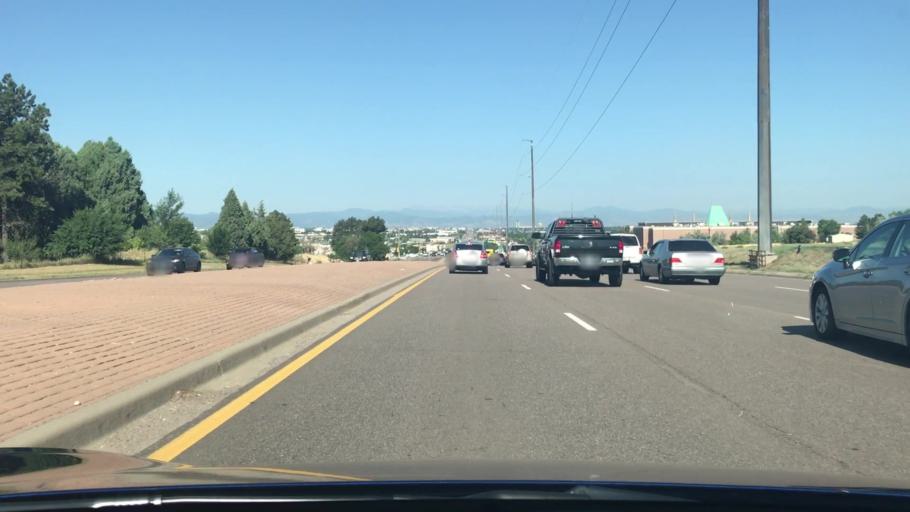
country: US
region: Colorado
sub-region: Arapahoe County
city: Dove Valley
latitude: 39.5951
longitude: -104.7927
